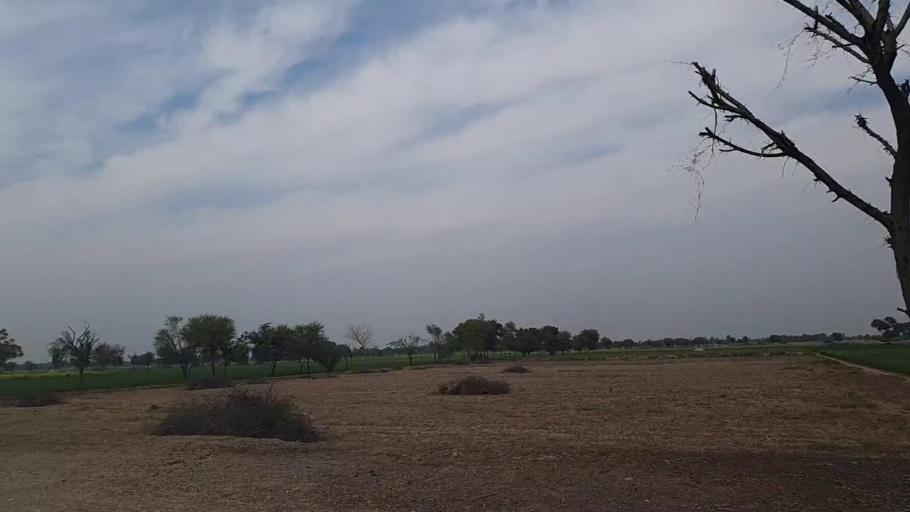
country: PK
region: Sindh
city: Daur
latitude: 26.4412
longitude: 68.4709
